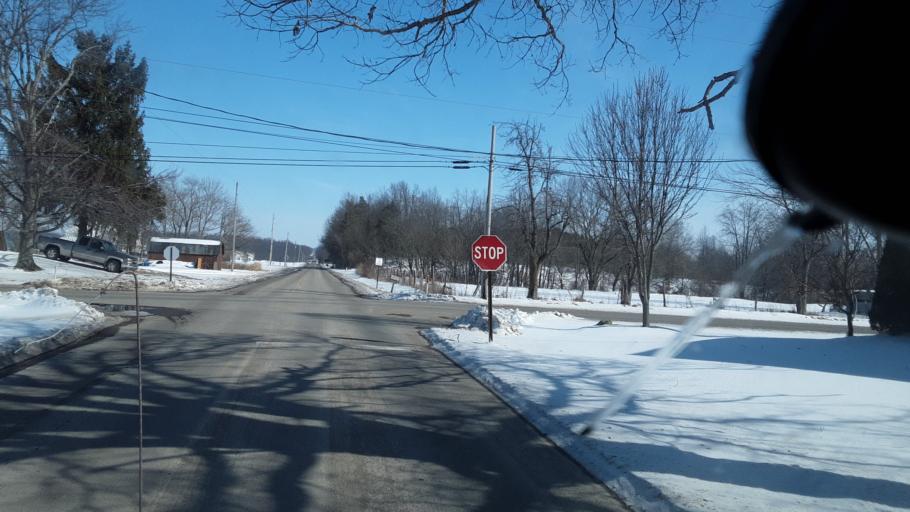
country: US
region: Ohio
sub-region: Mahoning County
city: Sebring
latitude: 40.9594
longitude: -81.0322
